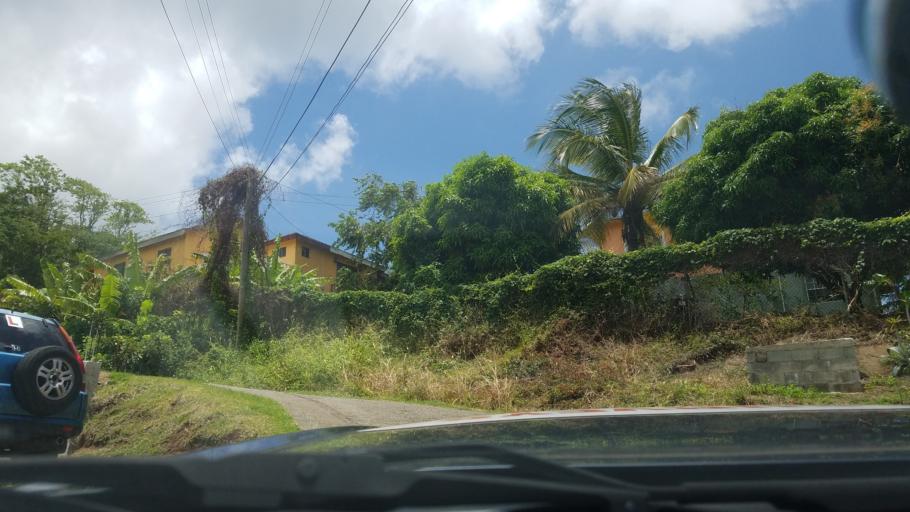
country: LC
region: Gros-Islet
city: Gros Islet
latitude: 14.0551
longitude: -60.9340
